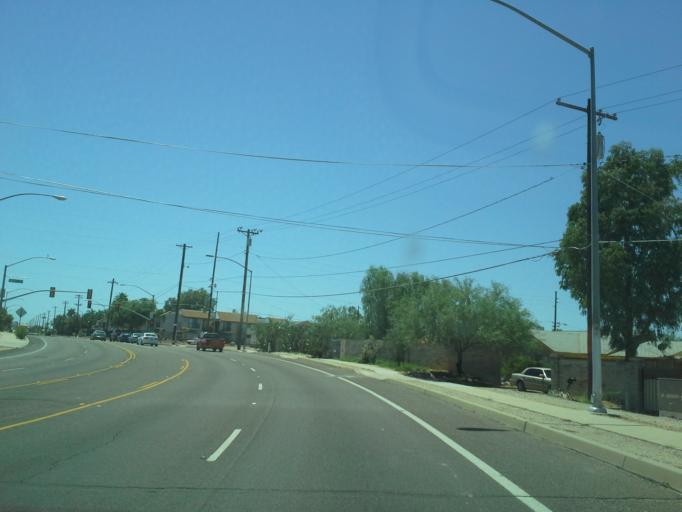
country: US
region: Arizona
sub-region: Pima County
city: Flowing Wells
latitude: 32.2802
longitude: -110.9721
